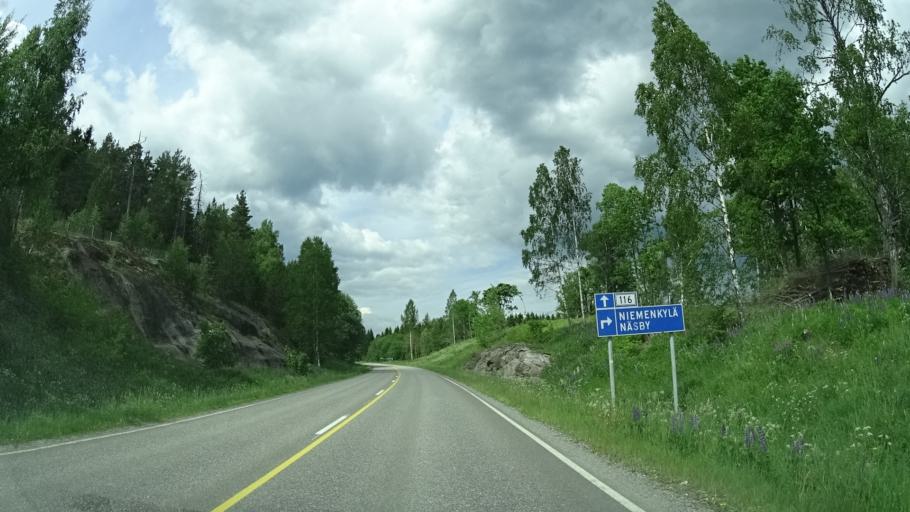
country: FI
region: Uusimaa
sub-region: Helsinki
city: Siuntio
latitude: 60.1888
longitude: 24.2034
